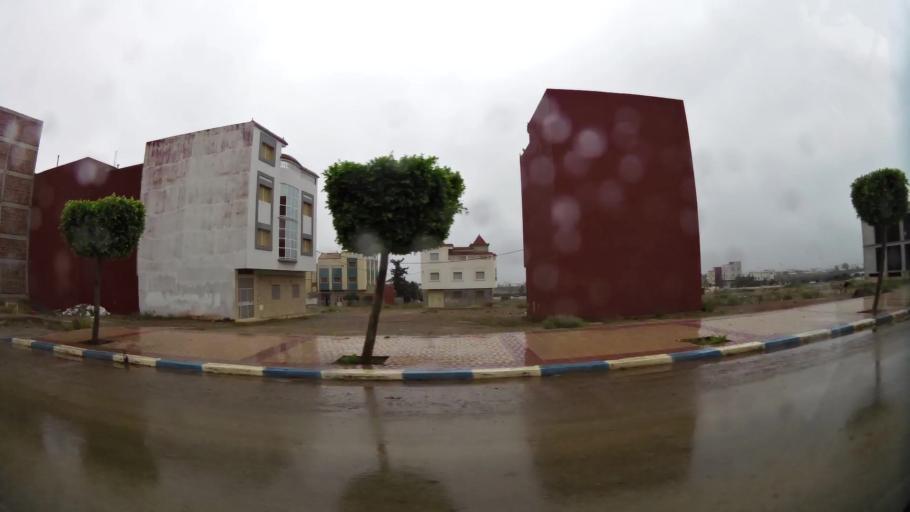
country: MA
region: Taza-Al Hoceima-Taounate
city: Imzourene
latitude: 35.1359
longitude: -3.8498
